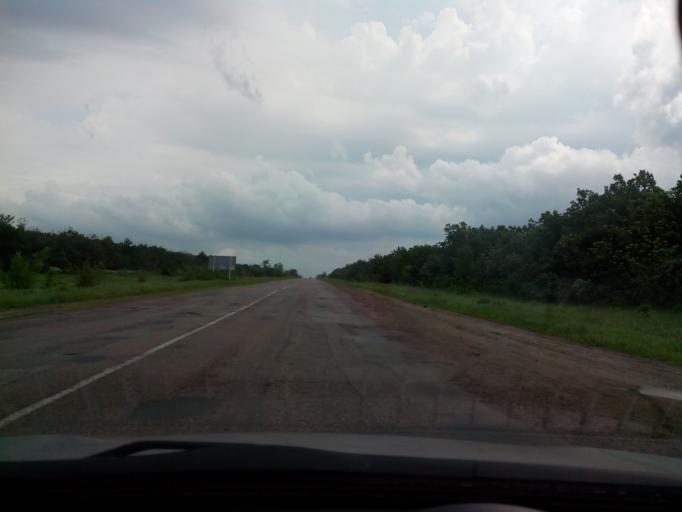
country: RU
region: Volgograd
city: Mikhaylovka
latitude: 49.9827
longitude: 43.0825
